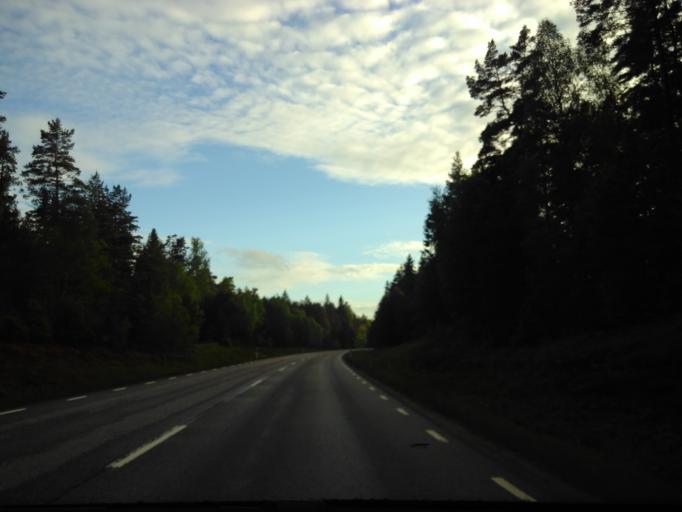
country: SE
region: Vaestra Goetaland
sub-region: Herrljunga Kommun
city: Herrljunga
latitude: 58.0624
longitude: 13.0749
